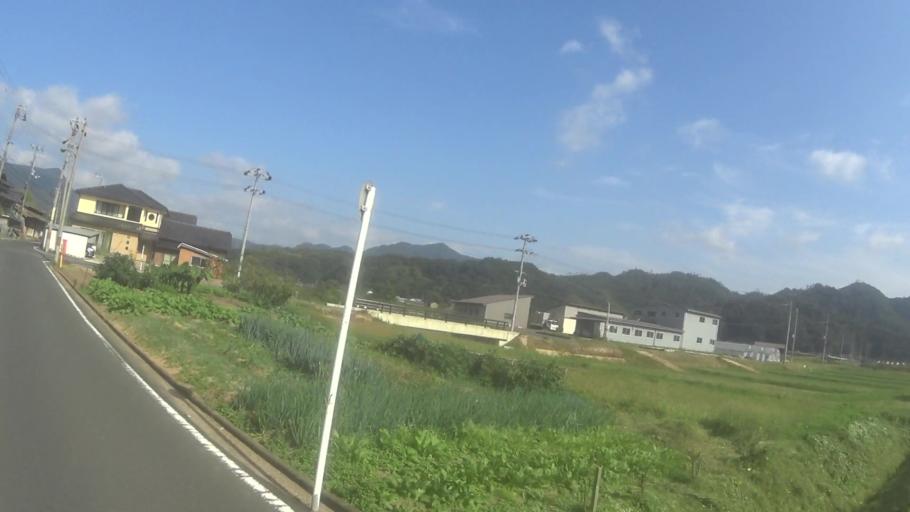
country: JP
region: Kyoto
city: Miyazu
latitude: 35.7096
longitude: 135.0994
